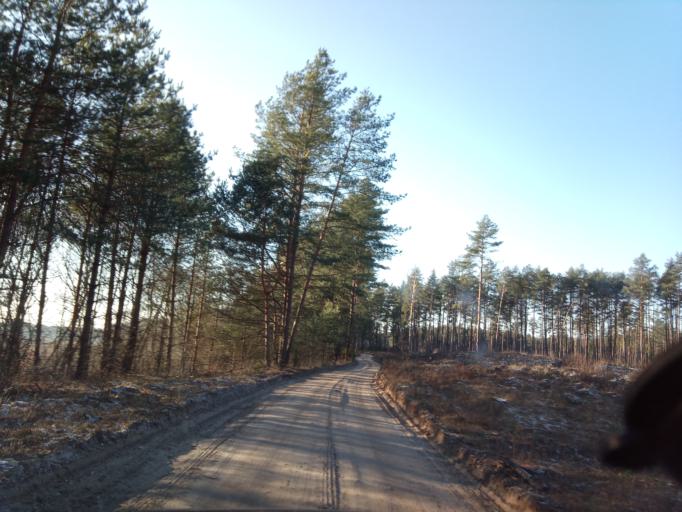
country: LT
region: Alytaus apskritis
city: Druskininkai
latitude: 53.9568
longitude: 23.8846
